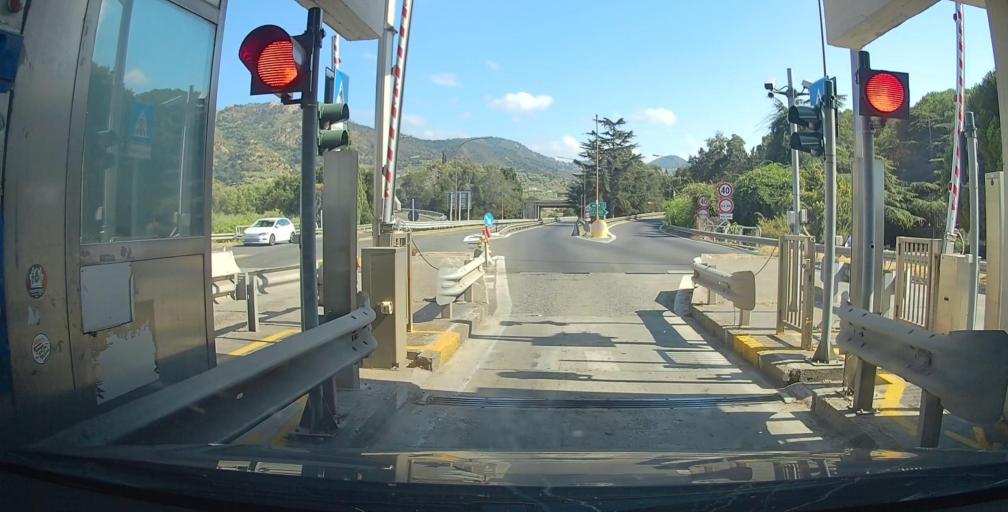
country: IT
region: Sicily
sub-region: Messina
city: Patti
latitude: 38.1452
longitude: 14.9991
